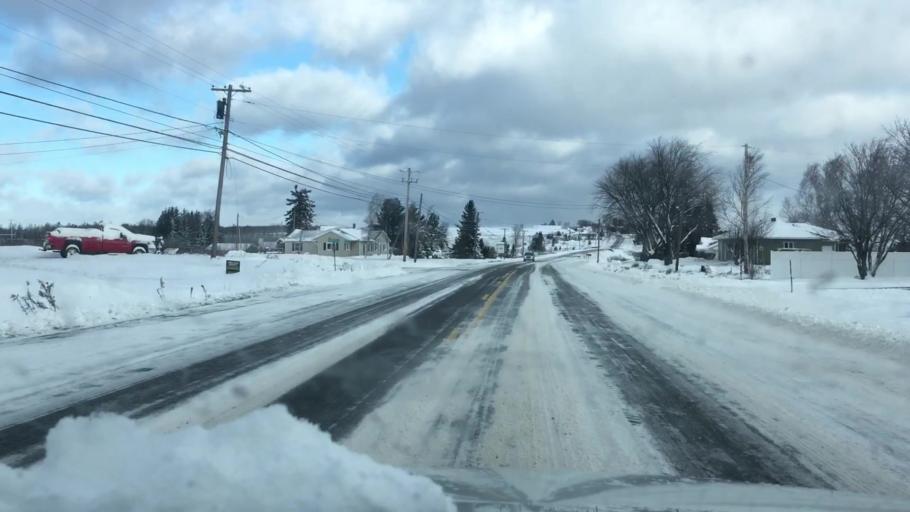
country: US
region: Maine
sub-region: Aroostook County
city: Caribou
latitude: 46.8932
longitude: -68.0156
